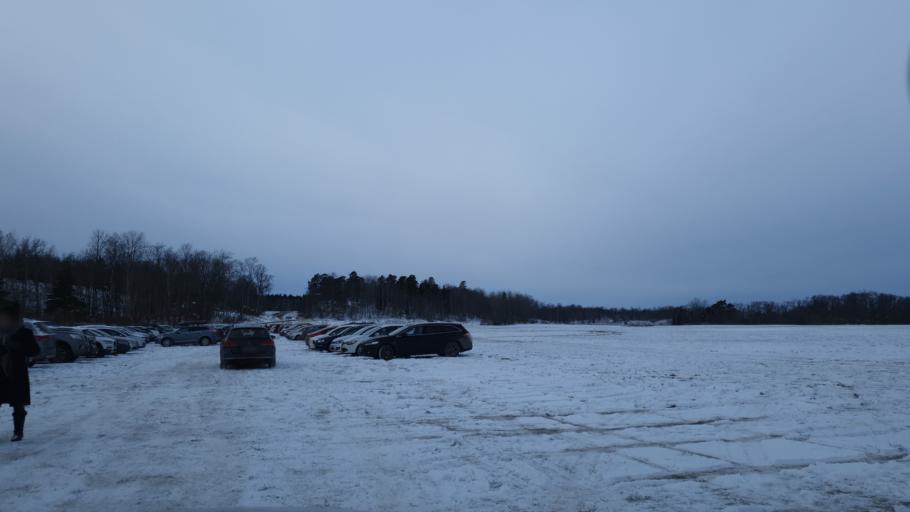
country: SE
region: Stockholm
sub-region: Sigtuna Kommun
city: Sigtuna
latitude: 59.7056
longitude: 17.6176
